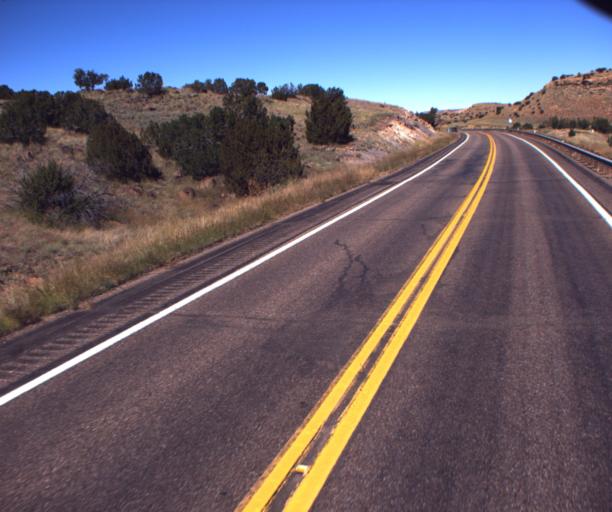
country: US
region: Arizona
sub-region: Apache County
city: Saint Johns
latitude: 34.3537
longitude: -109.3787
